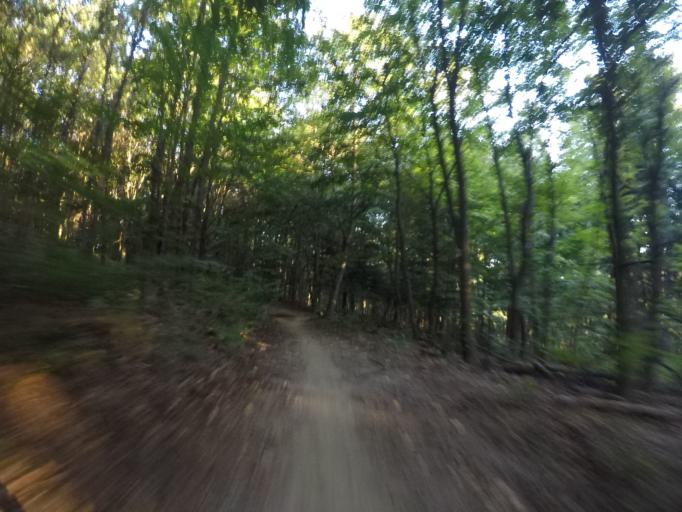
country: SK
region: Kosicky
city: Kosice
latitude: 48.7498
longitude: 21.1879
